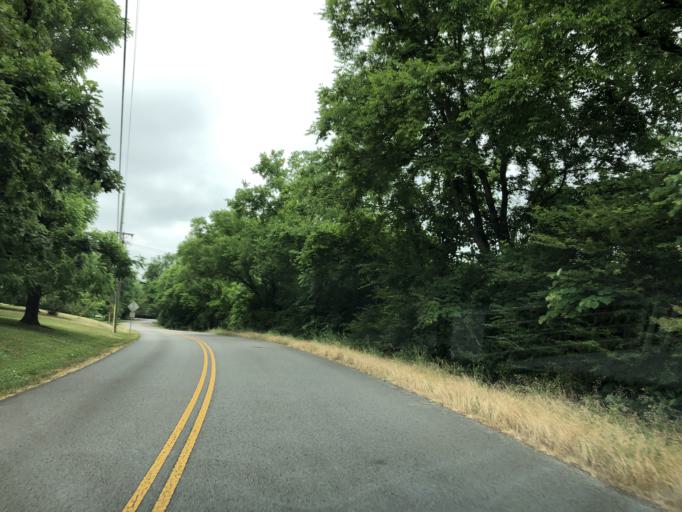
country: US
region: Tennessee
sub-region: Davidson County
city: Goodlettsville
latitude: 36.2890
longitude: -86.7312
